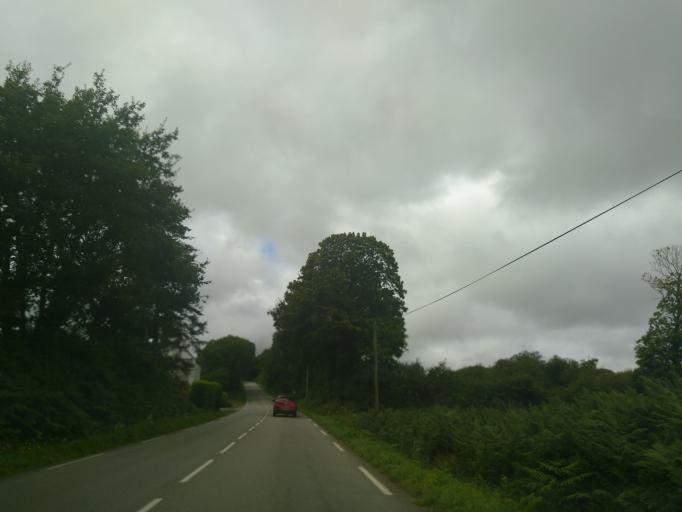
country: FR
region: Brittany
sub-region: Departement du Finistere
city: Poullan-sur-Mer
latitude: 48.0544
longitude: -4.3918
